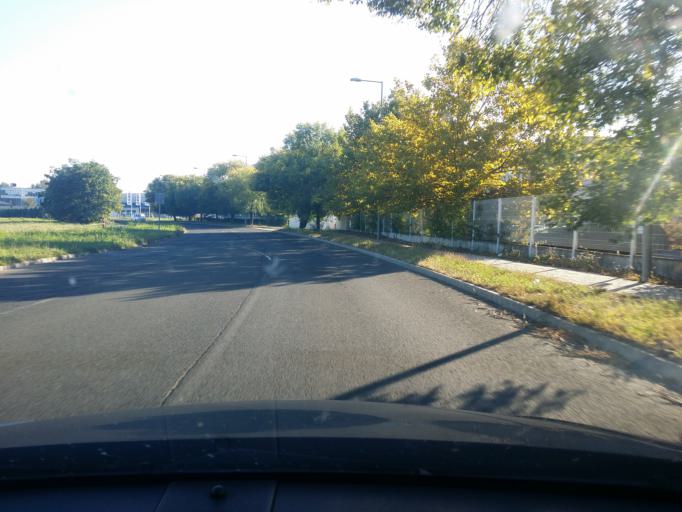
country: HU
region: Budapest
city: Budapest XV. keruelet
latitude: 47.5958
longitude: 19.1060
